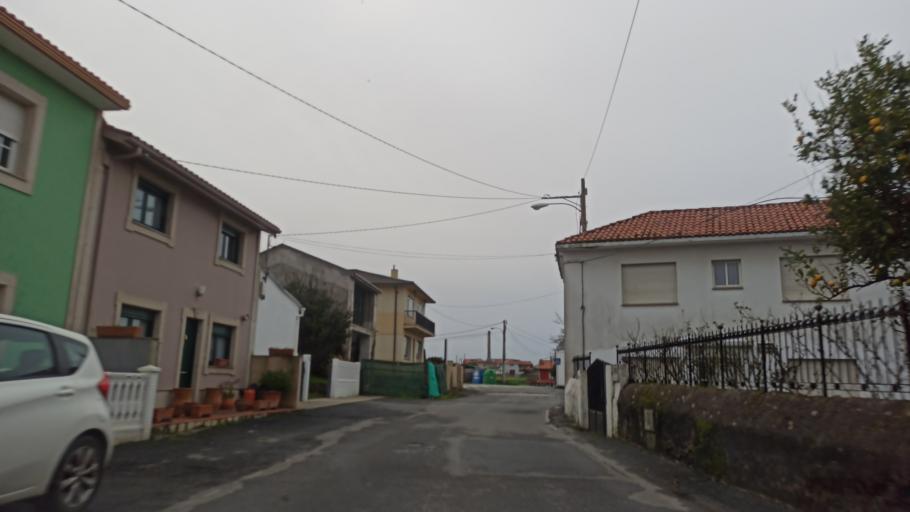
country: ES
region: Galicia
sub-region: Provincia da Coruna
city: Oleiros
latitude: 43.3954
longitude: -8.3222
